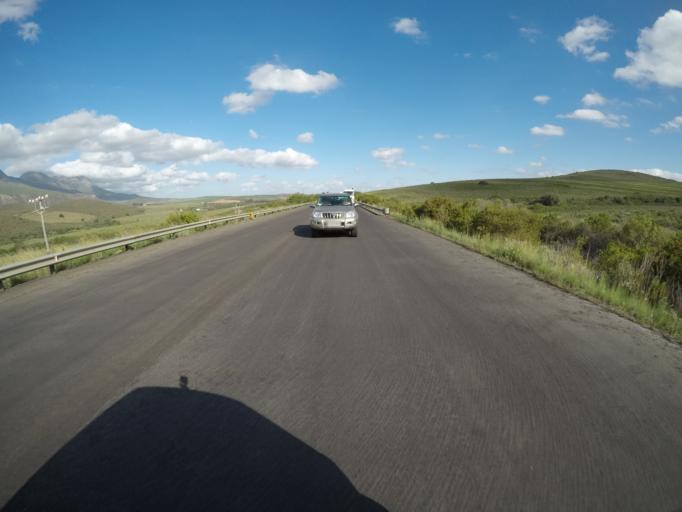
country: ZA
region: Western Cape
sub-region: Cape Winelands District Municipality
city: Ashton
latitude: -33.9313
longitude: 20.2090
